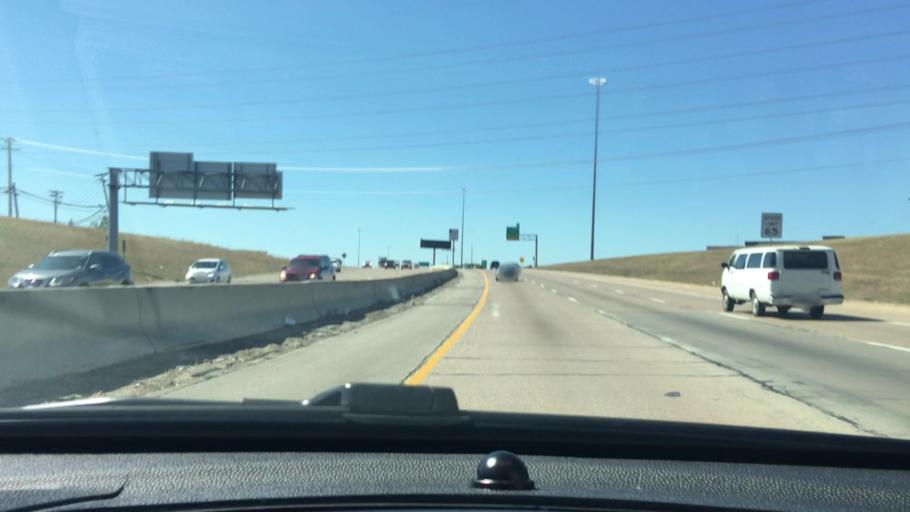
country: US
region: Texas
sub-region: Dallas County
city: Cockrell Hill
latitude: 32.7013
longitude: -96.8244
